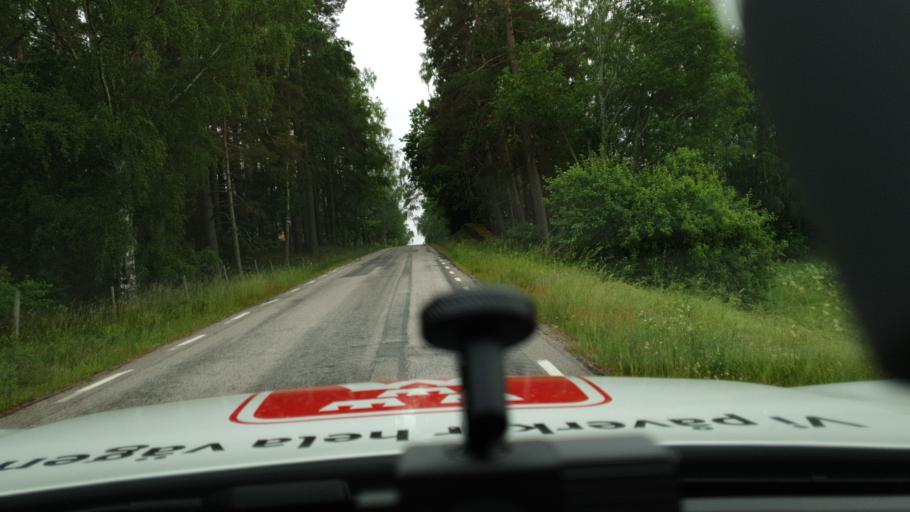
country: SE
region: Vaestra Goetaland
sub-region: Skovde Kommun
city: Stopen
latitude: 58.5447
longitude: 13.8677
